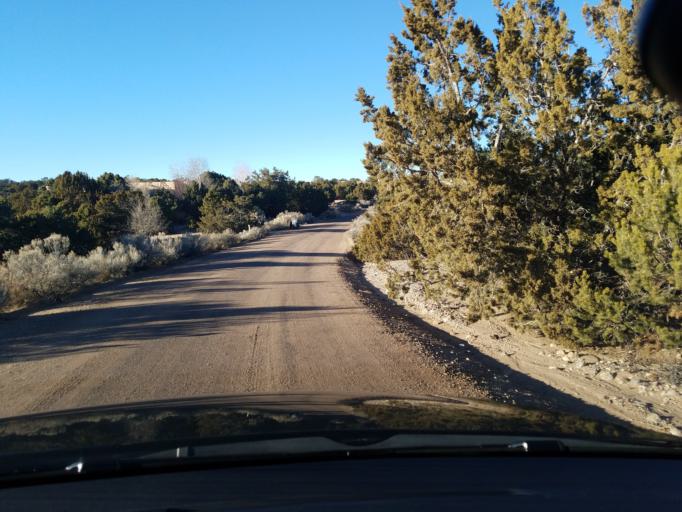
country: US
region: New Mexico
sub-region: Santa Fe County
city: Agua Fria
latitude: 35.6736
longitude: -105.9988
